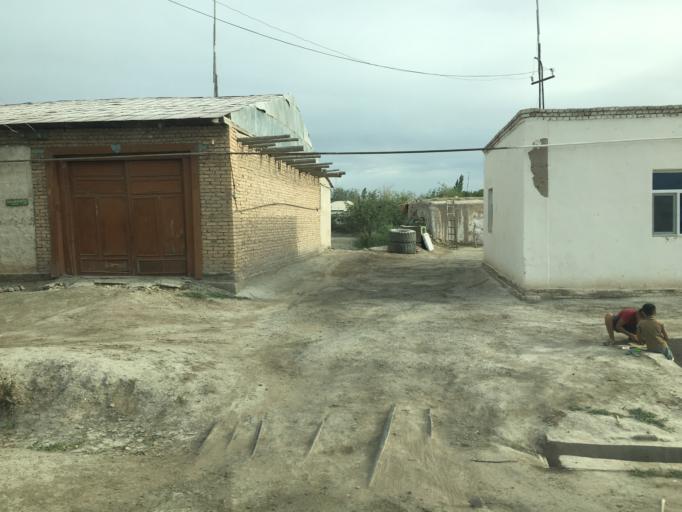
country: TM
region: Dasoguz
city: Dasoguz
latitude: 41.8203
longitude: 59.9186
